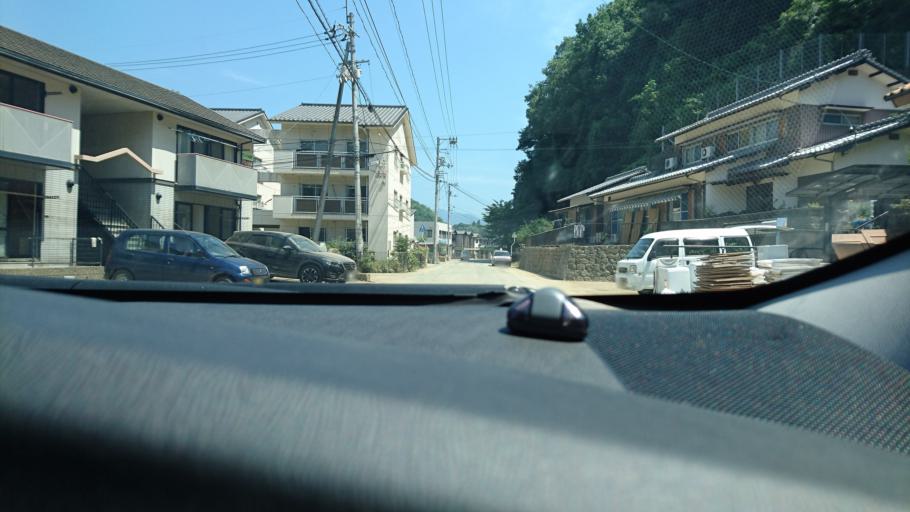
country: JP
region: Ehime
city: Ozu
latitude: 33.5001
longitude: 132.5476
